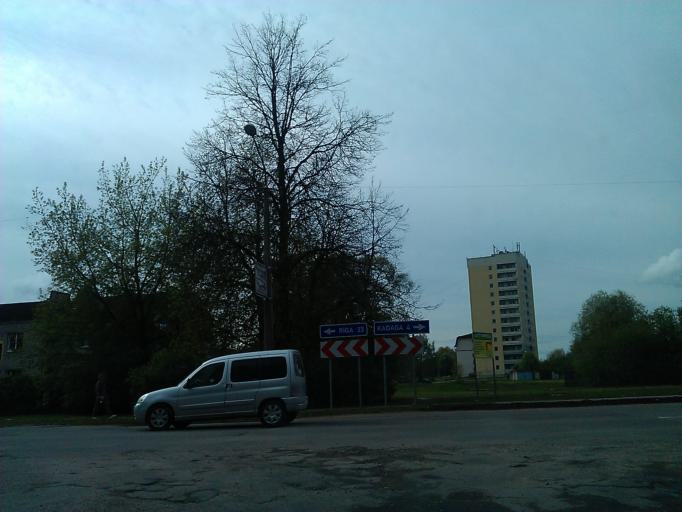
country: LV
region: Adazi
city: Adazi
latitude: 57.0778
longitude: 24.3272
